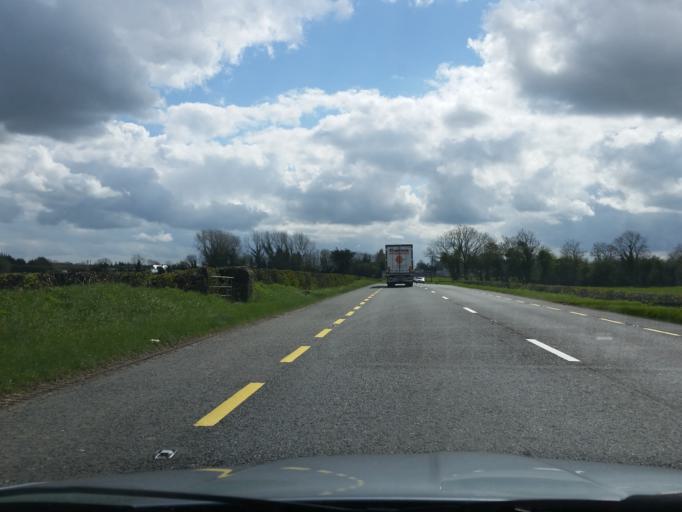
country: IE
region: Leinster
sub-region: An Mhi
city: Ratoath
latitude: 53.5776
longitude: -6.4536
